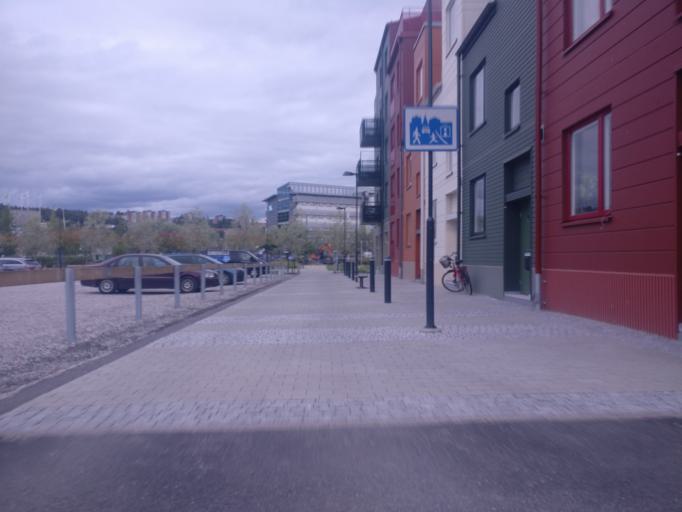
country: SE
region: Vaesternorrland
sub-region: Sundsvalls Kommun
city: Sundsvall
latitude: 62.3888
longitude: 17.3173
